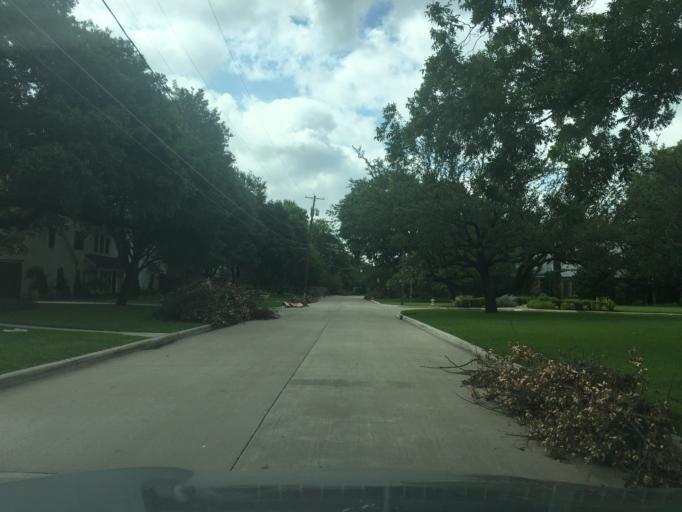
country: US
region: Texas
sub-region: Dallas County
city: Addison
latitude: 32.9113
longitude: -96.8224
